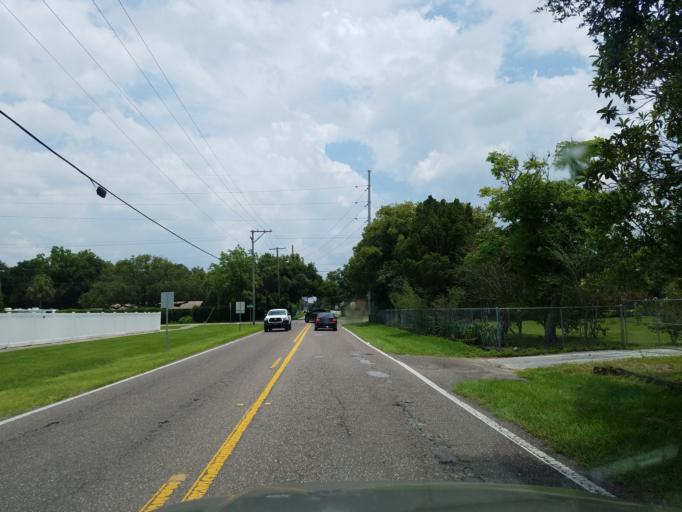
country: US
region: Florida
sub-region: Hillsborough County
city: Valrico
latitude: 27.9232
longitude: -82.2371
